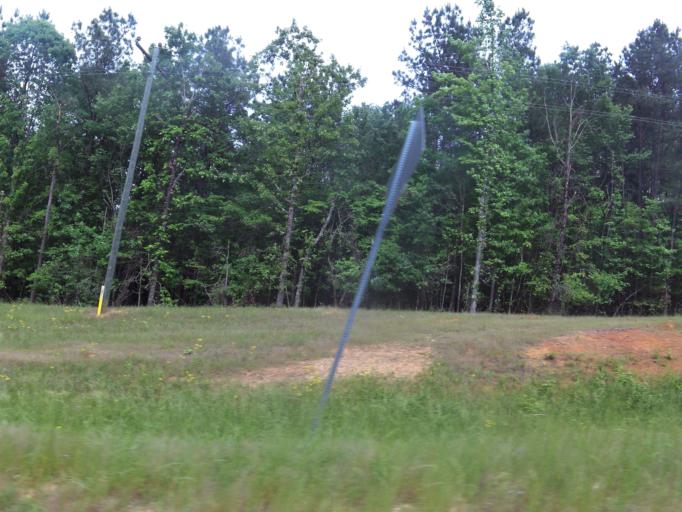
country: US
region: Georgia
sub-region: McDuffie County
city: Thomson
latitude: 33.3380
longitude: -82.4571
